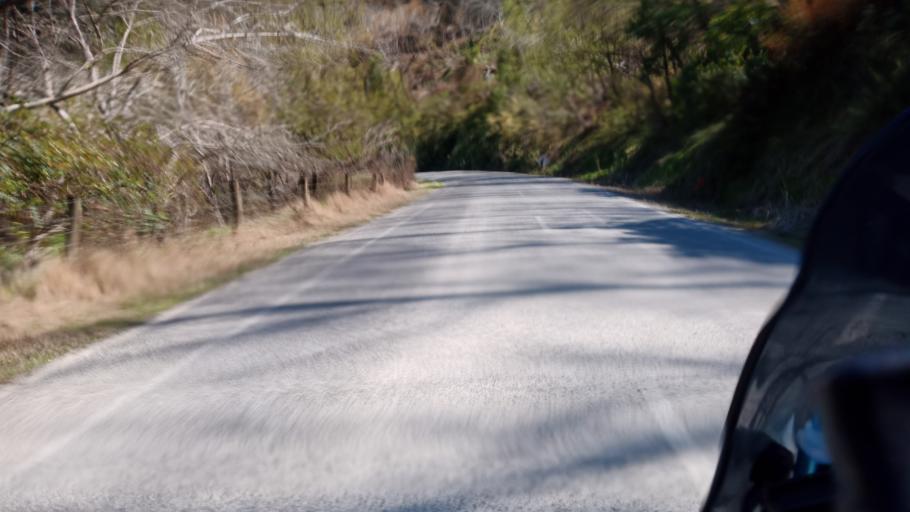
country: NZ
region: Gisborne
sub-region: Gisborne District
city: Gisborne
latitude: -38.7694
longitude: 177.8071
